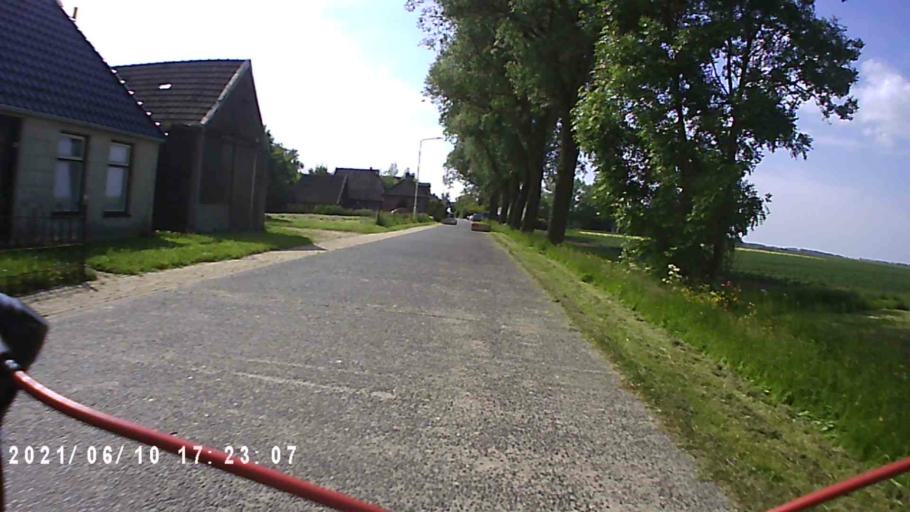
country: NL
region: Friesland
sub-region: Gemeente Kollumerland en Nieuwkruisland
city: Kollum
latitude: 53.2963
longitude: 6.2310
